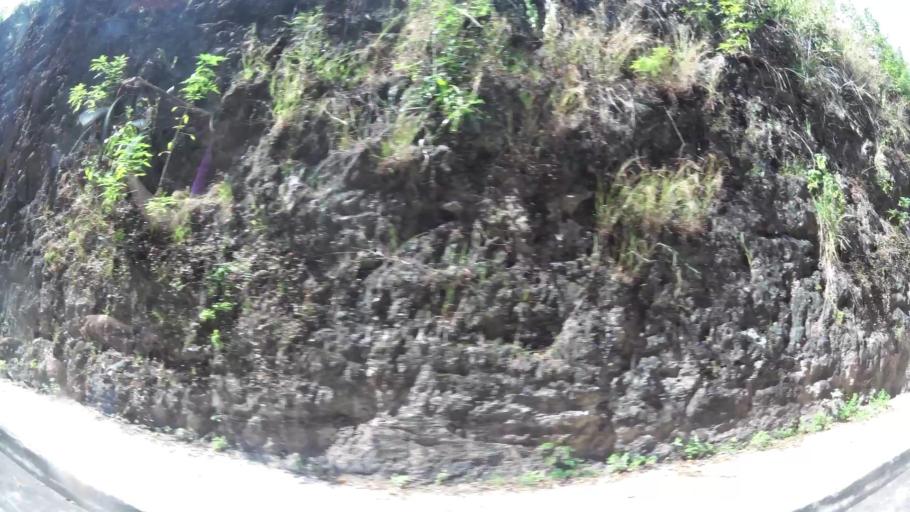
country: MQ
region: Martinique
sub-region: Martinique
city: Saint-Pierre
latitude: 14.6930
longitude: -61.1630
